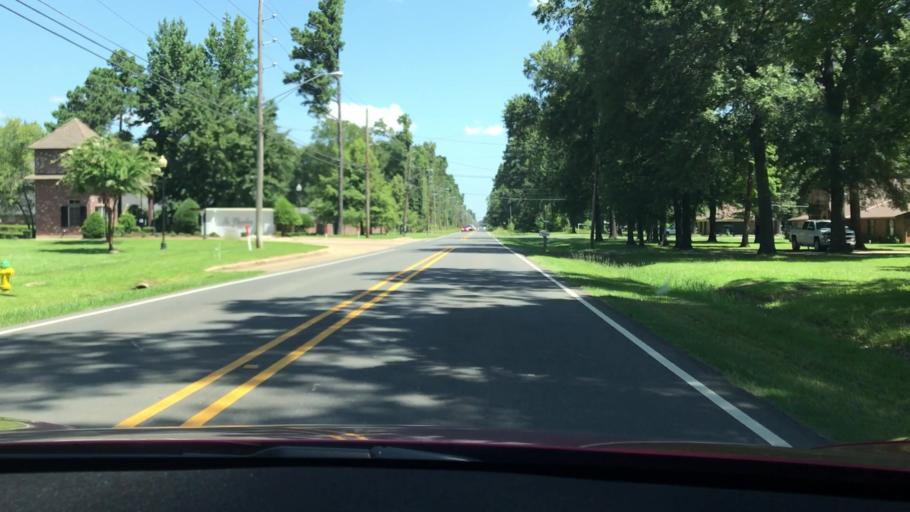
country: US
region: Louisiana
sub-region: De Soto Parish
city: Stonewall
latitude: 32.3456
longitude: -93.7138
